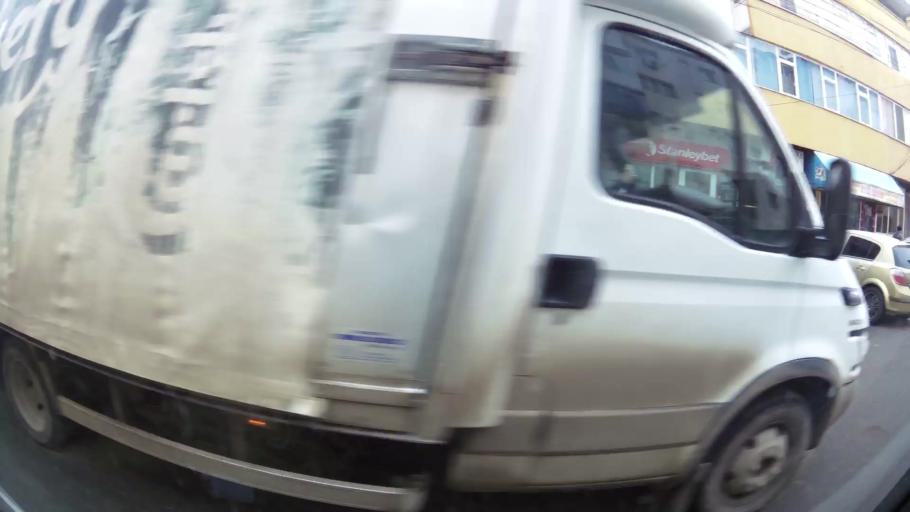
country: RO
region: Prahova
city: Ploiesti
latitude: 44.9397
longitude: 26.0464
